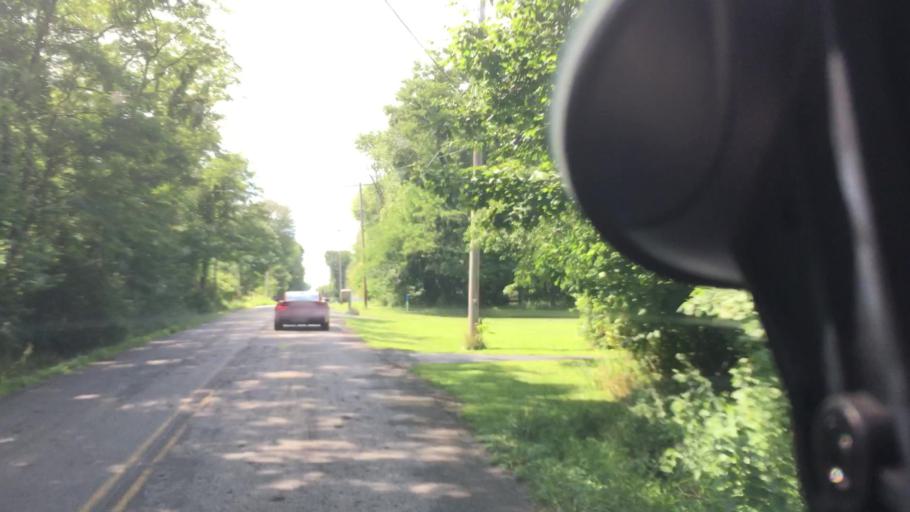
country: US
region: Pennsylvania
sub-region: Mercer County
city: Reynolds Heights
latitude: 41.3146
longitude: -80.3992
